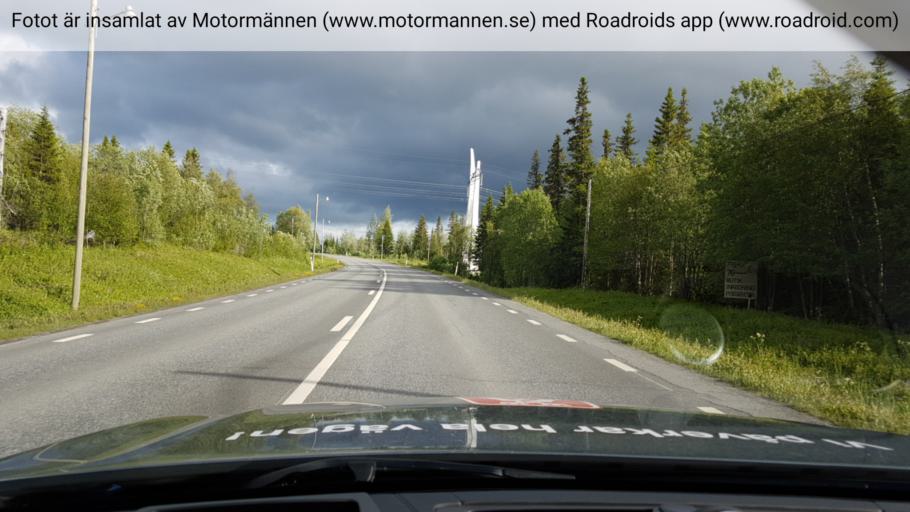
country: SE
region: Jaemtland
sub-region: Are Kommun
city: Are
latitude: 63.3470
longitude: 13.1908
